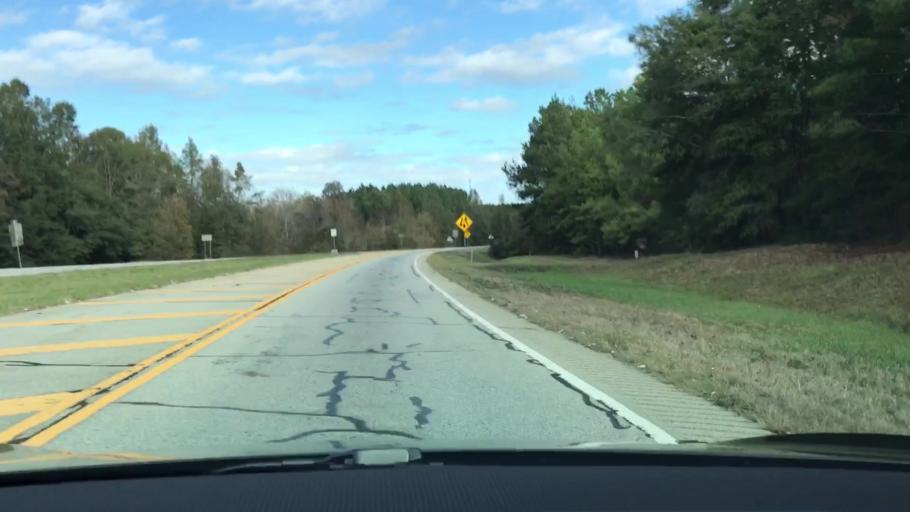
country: US
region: Georgia
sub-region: Jefferson County
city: Wadley
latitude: 32.8927
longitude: -82.4010
